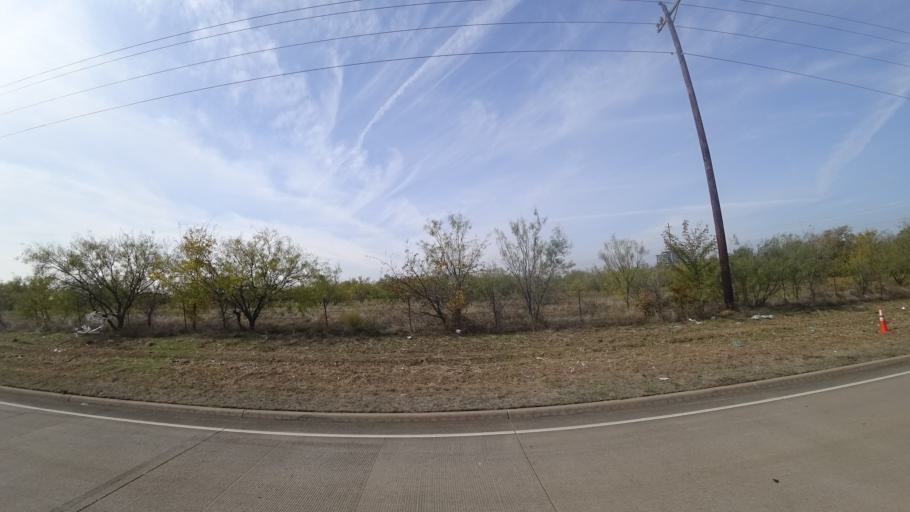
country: US
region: Texas
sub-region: Denton County
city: The Colony
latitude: 33.0584
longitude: -96.8855
